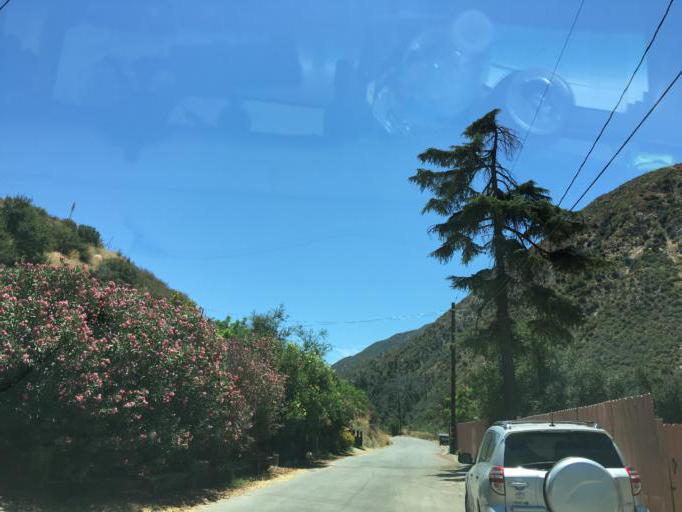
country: US
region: California
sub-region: Los Angeles County
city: La Crescenta-Montrose
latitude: 34.2897
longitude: -118.2323
